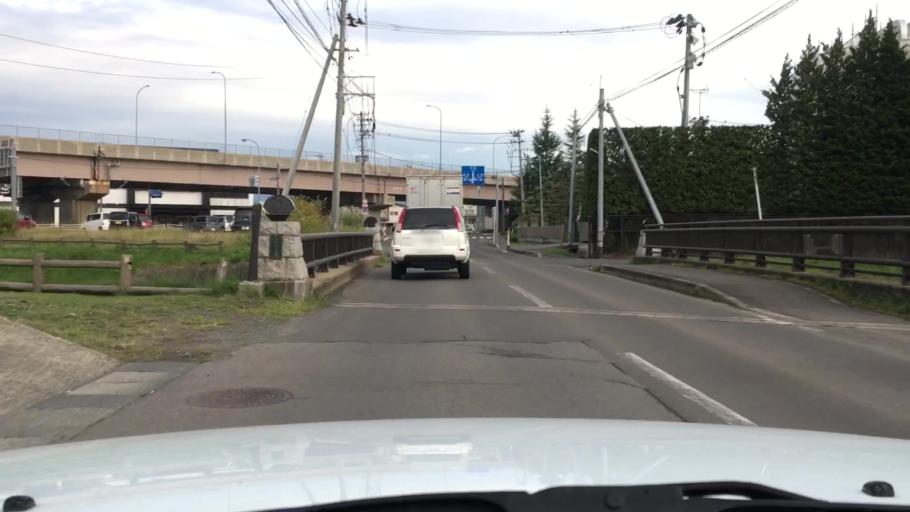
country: JP
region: Aomori
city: Hirosaki
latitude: 40.5960
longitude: 140.5024
